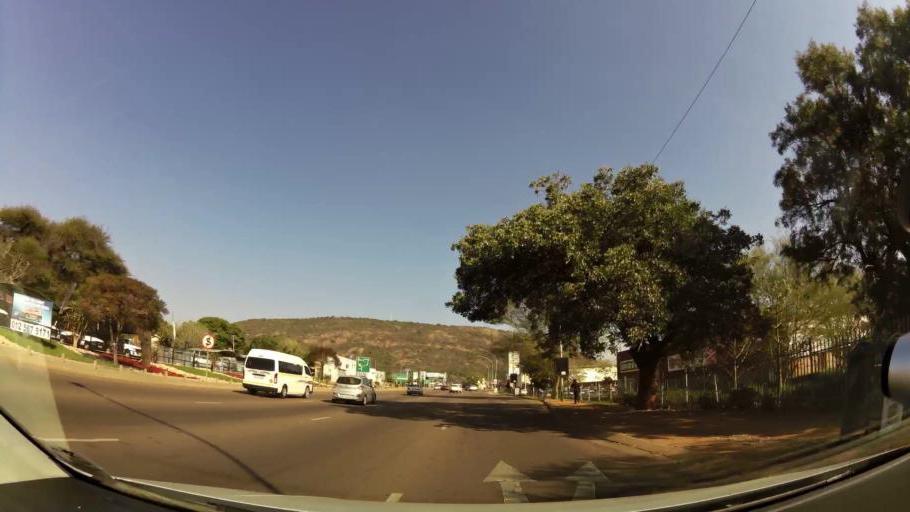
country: ZA
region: Gauteng
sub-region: City of Tshwane Metropolitan Municipality
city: Pretoria
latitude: -25.6815
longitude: 28.1938
